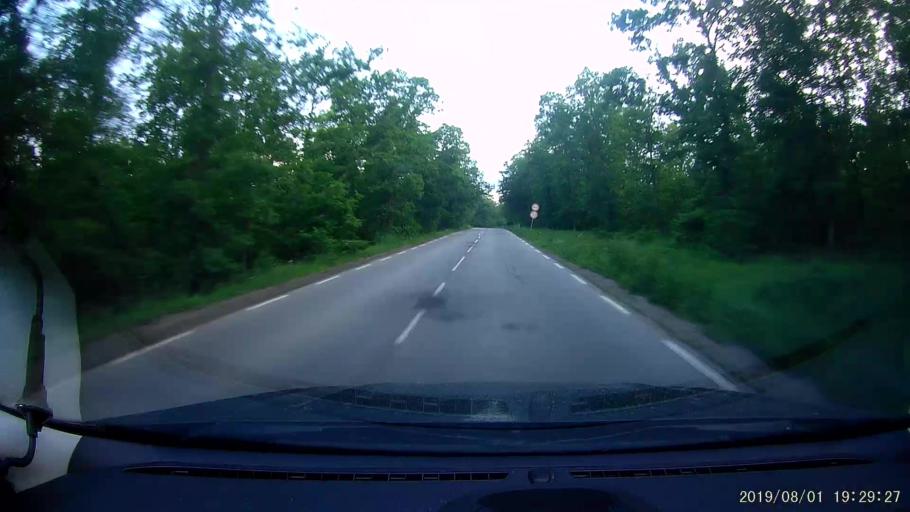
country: BG
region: Burgas
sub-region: Obshtina Sungurlare
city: Sungurlare
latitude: 42.8256
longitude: 26.9072
